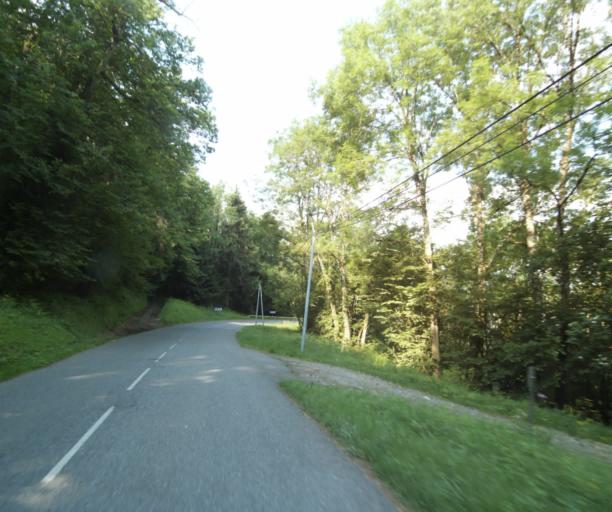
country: FR
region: Rhone-Alpes
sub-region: Departement de la Haute-Savoie
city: Allinges
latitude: 46.3108
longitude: 6.4946
